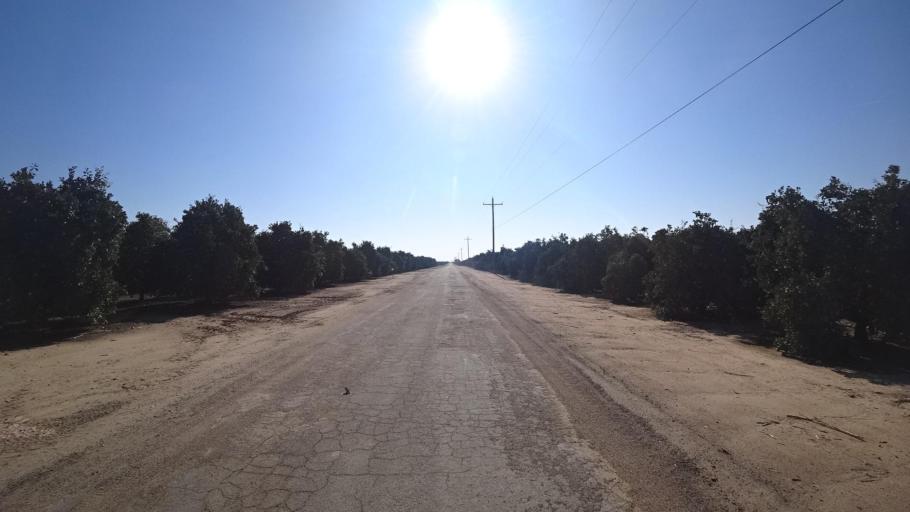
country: US
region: California
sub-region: Tulare County
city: Richgrove
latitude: 35.7235
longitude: -119.1429
